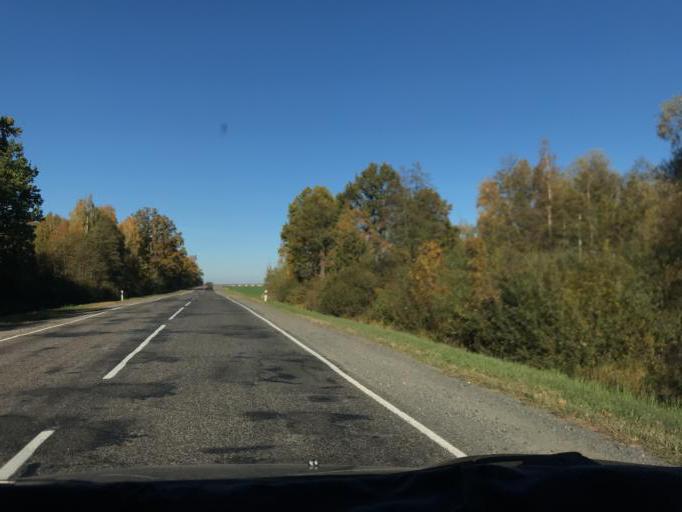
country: BY
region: Gomel
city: Yel'sk
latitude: 51.7404
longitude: 29.1755
